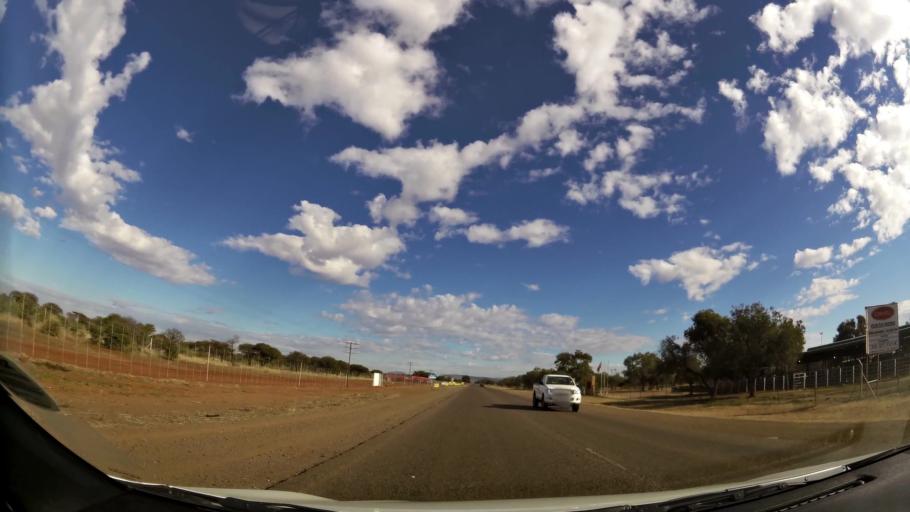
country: ZA
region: Limpopo
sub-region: Waterberg District Municipality
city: Bela-Bela
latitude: -24.9153
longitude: 28.3640
